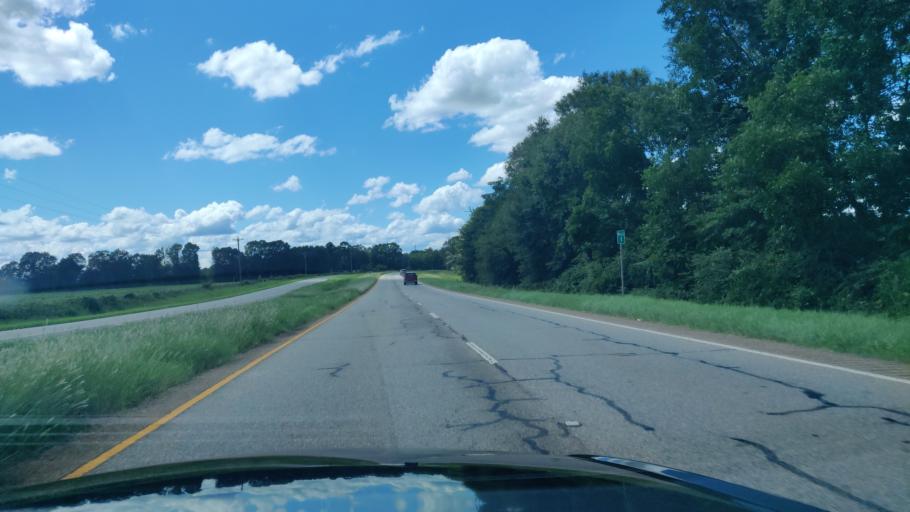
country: US
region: Georgia
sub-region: Stewart County
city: Richland
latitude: 31.9988
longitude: -84.6441
